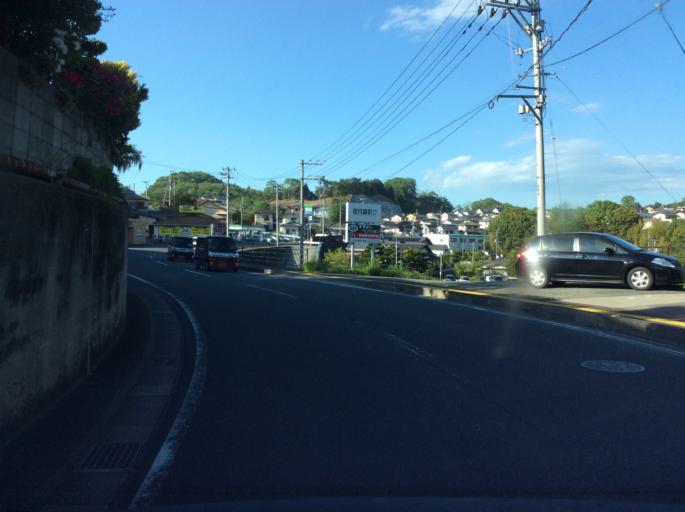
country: JP
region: Fukushima
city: Iwaki
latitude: 37.0006
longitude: 140.8392
